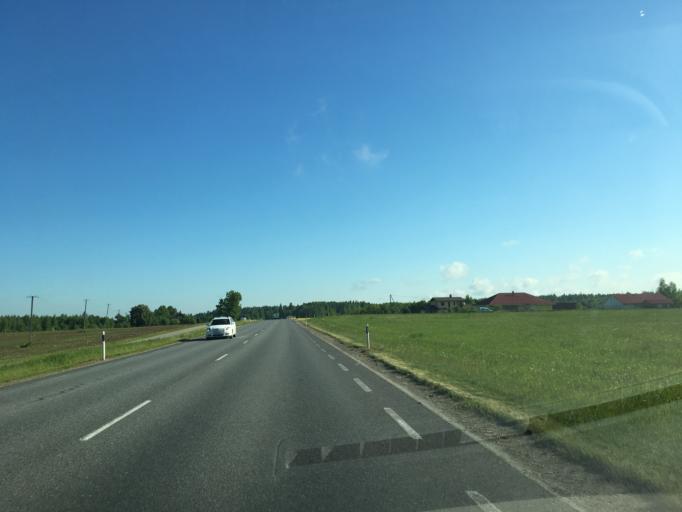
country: EE
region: Tartu
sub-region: Tartu linn
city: Tartu
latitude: 58.4377
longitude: 26.6813
